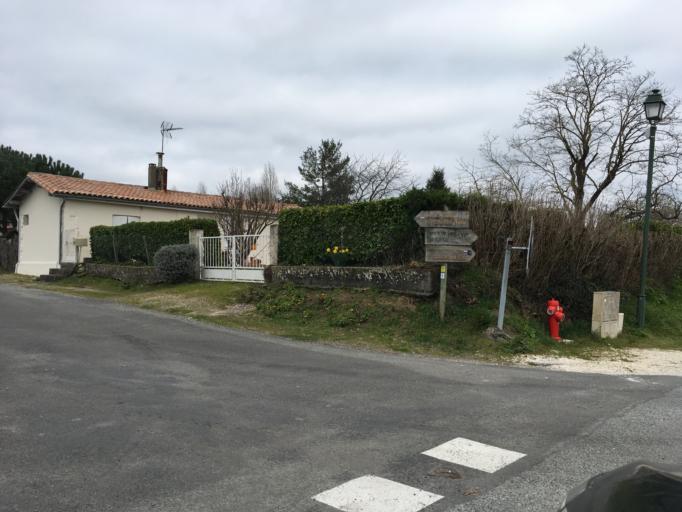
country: FR
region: Aquitaine
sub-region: Departement de la Gironde
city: Saint-Ciers-sur-Gironde
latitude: 45.3138
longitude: -0.5895
